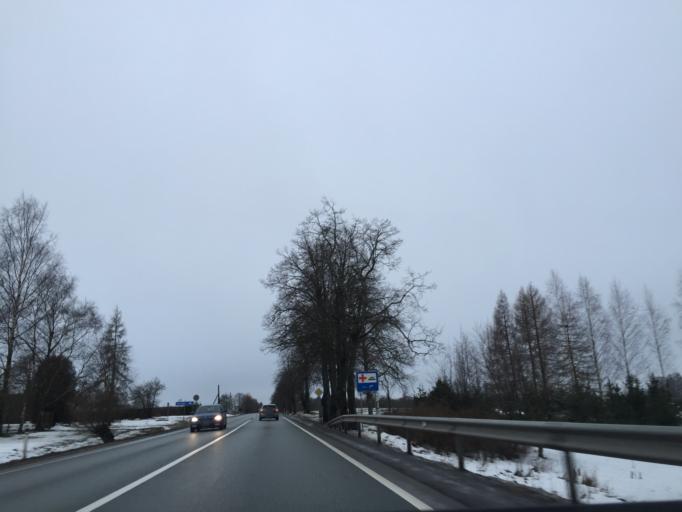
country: LV
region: Krimulda
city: Ragana
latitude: 57.1753
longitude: 24.7085
